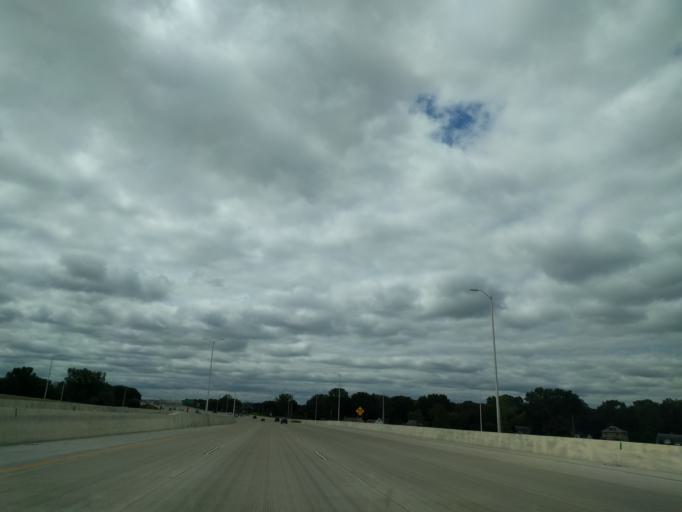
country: US
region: Wisconsin
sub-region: Brown County
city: Howard
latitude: 44.5568
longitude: -88.0605
